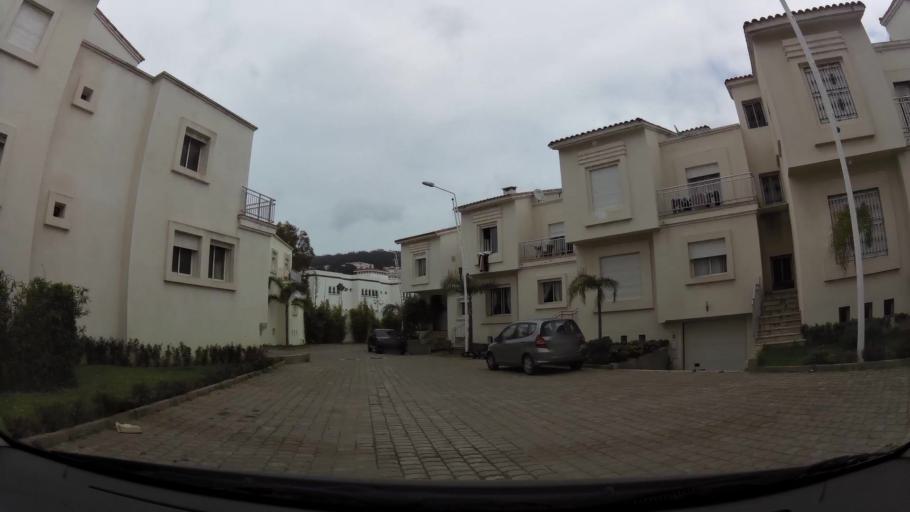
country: MA
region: Tanger-Tetouan
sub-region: Tanger-Assilah
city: Boukhalef
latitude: 35.7749
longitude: -5.8591
